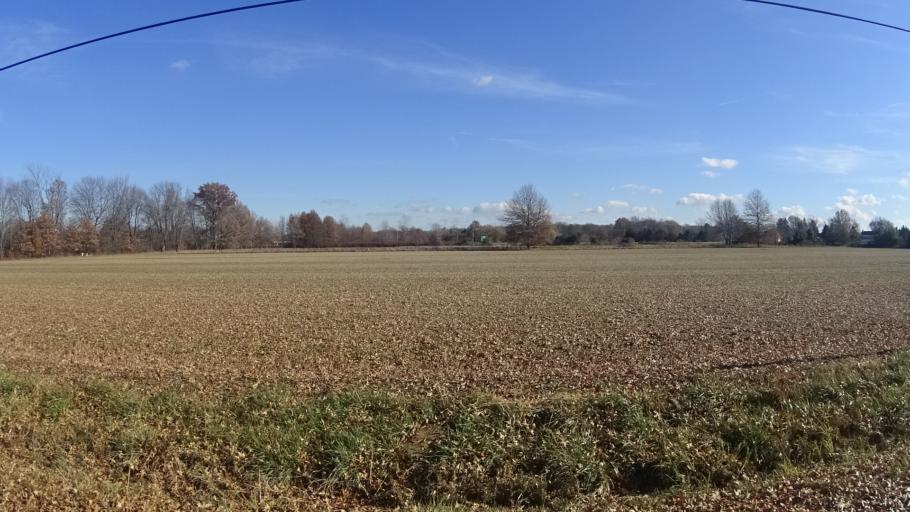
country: US
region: Ohio
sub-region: Lorain County
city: North Ridgeville
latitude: 41.3509
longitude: -82.0352
